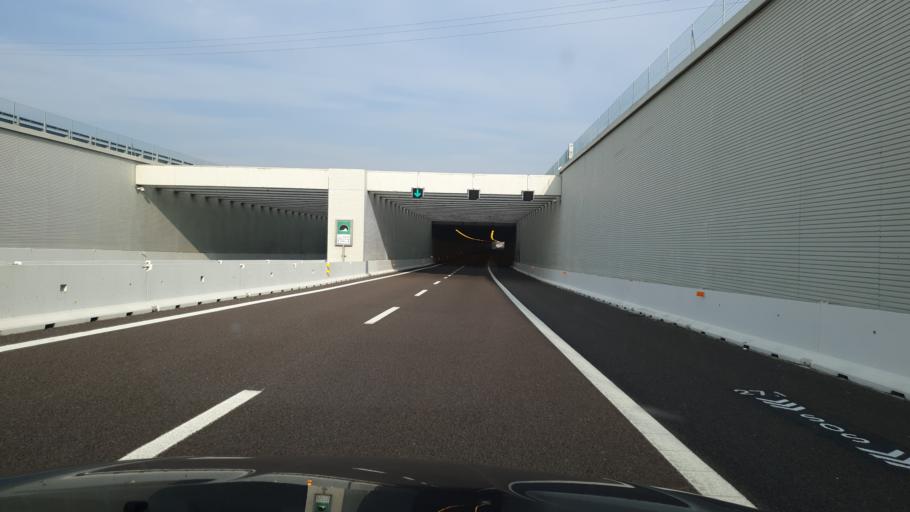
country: IT
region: Veneto
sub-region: Provincia di Vicenza
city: Noventa Vicentina
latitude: 45.2933
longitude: 11.5745
